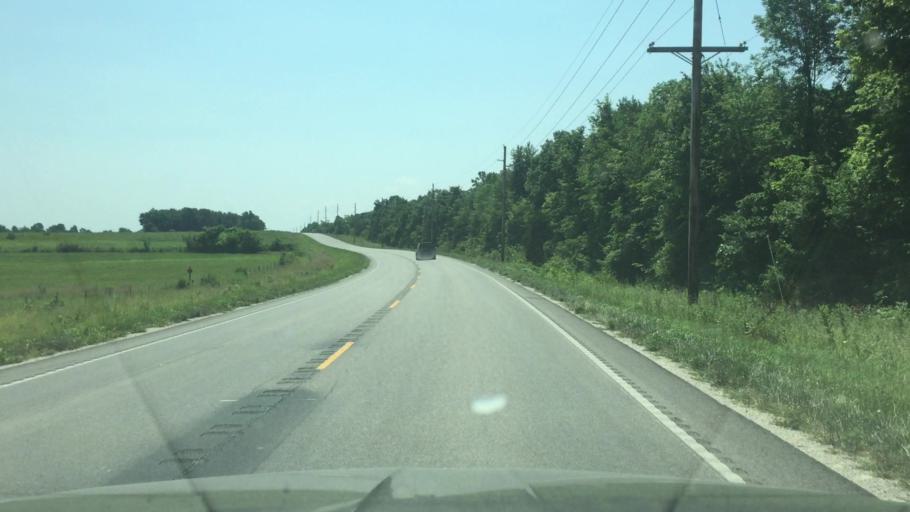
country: US
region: Missouri
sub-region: Miller County
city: Eldon
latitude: 38.3898
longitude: -92.7045
